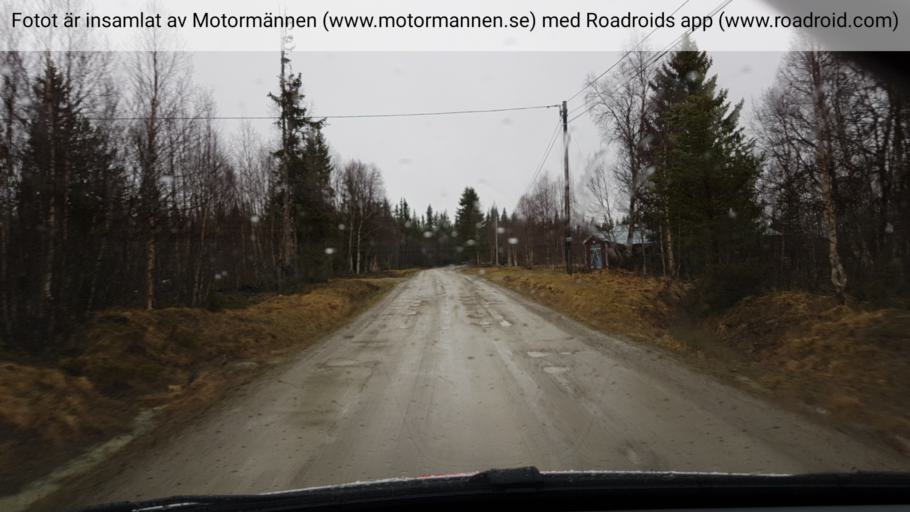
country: SE
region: Jaemtland
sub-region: Are Kommun
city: Jarpen
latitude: 62.5672
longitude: 13.4059
